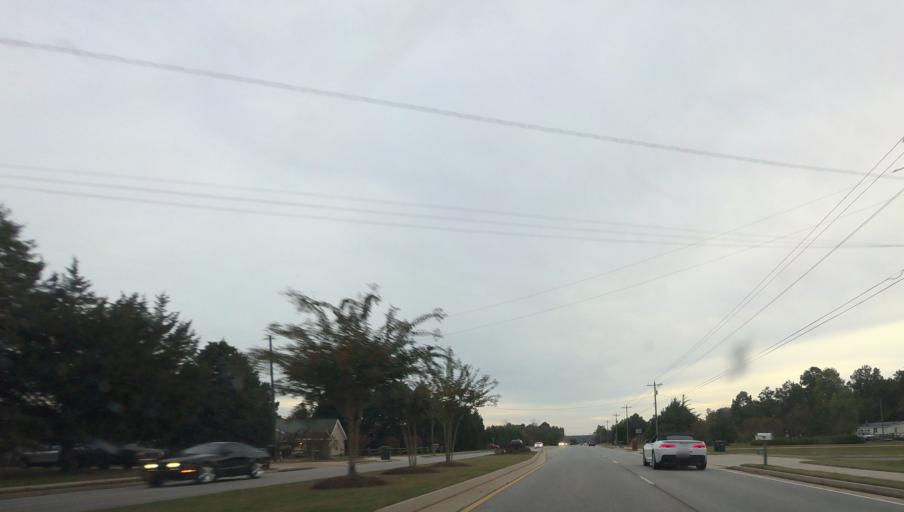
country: US
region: Georgia
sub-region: Houston County
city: Perry
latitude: 32.5145
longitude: -83.6625
